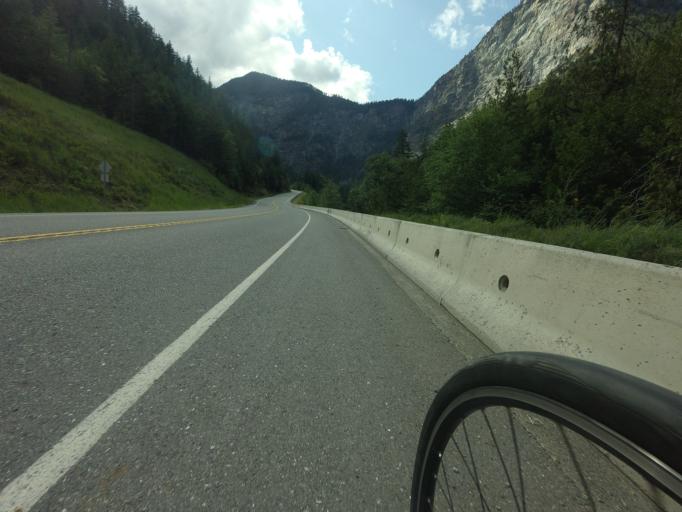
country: CA
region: British Columbia
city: Lillooet
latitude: 50.6444
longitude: -122.0552
